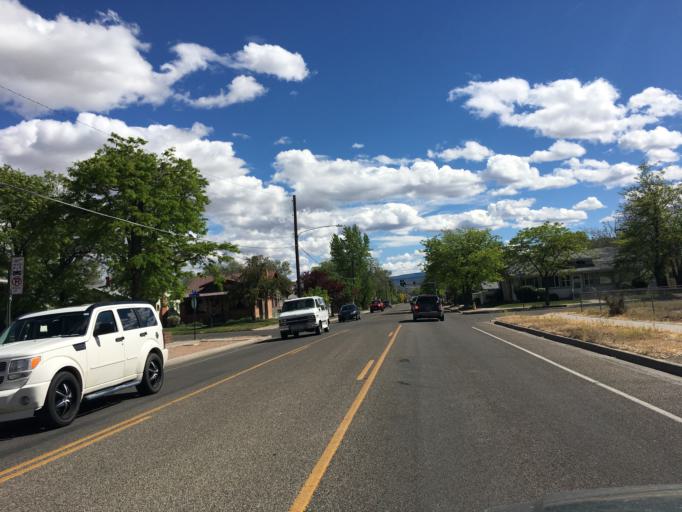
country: US
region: Colorado
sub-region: Mesa County
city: Grand Junction
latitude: 39.0718
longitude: -108.5524
